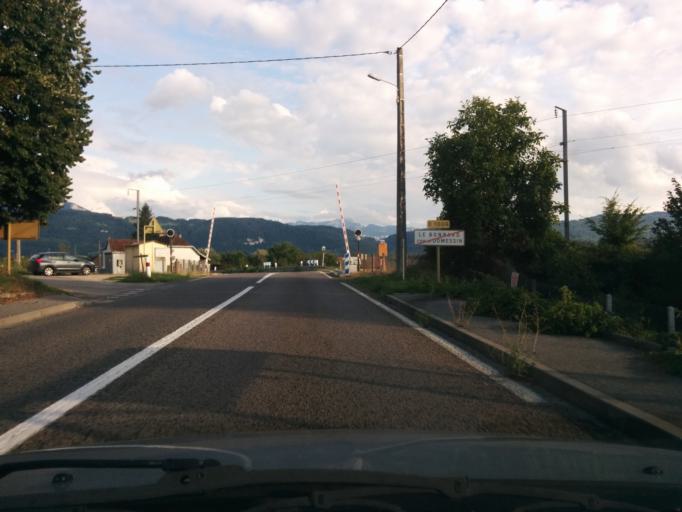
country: FR
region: Rhone-Alpes
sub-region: Departement de la Savoie
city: Domessin
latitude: 45.5249
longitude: 5.6951
